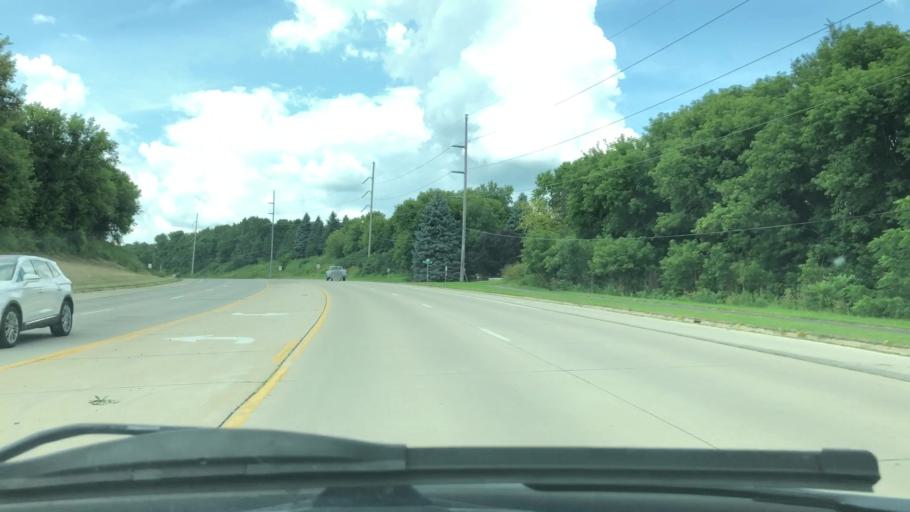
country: US
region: Minnesota
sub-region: Olmsted County
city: Rochester
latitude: 44.0101
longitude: -92.5094
